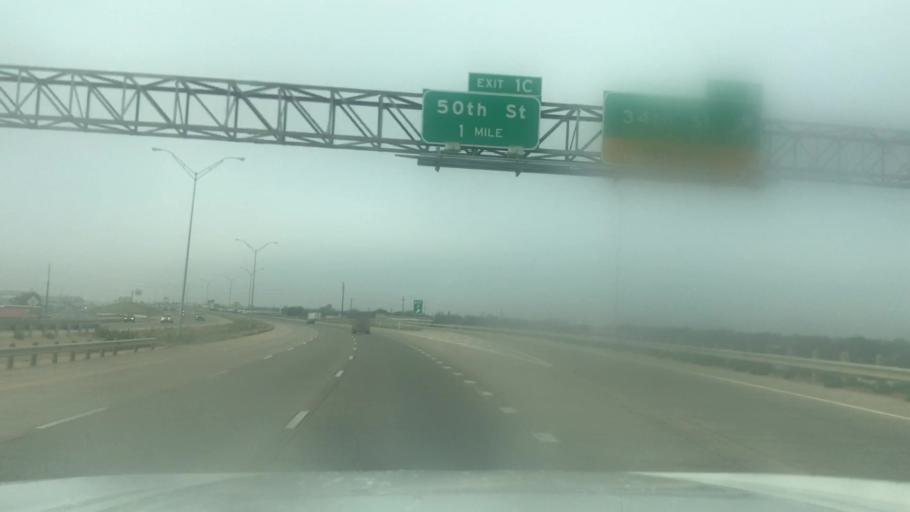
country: US
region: Texas
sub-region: Lubbock County
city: Lubbock
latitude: 33.5709
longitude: -101.8445
